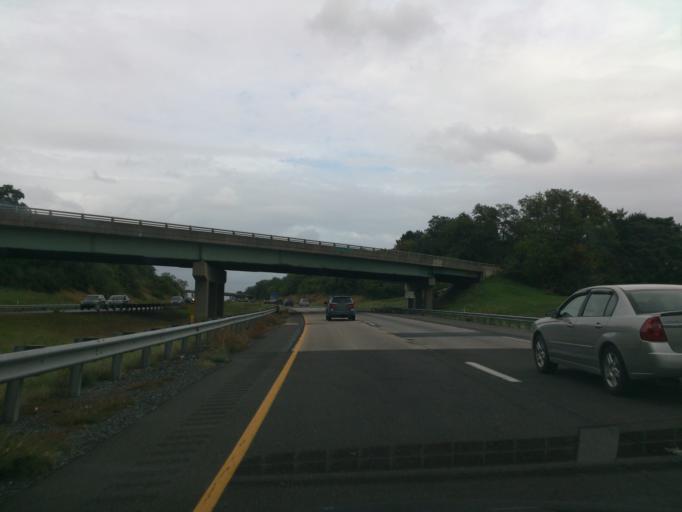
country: US
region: Pennsylvania
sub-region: Lancaster County
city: Brownstown
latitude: 40.1201
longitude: -76.2248
